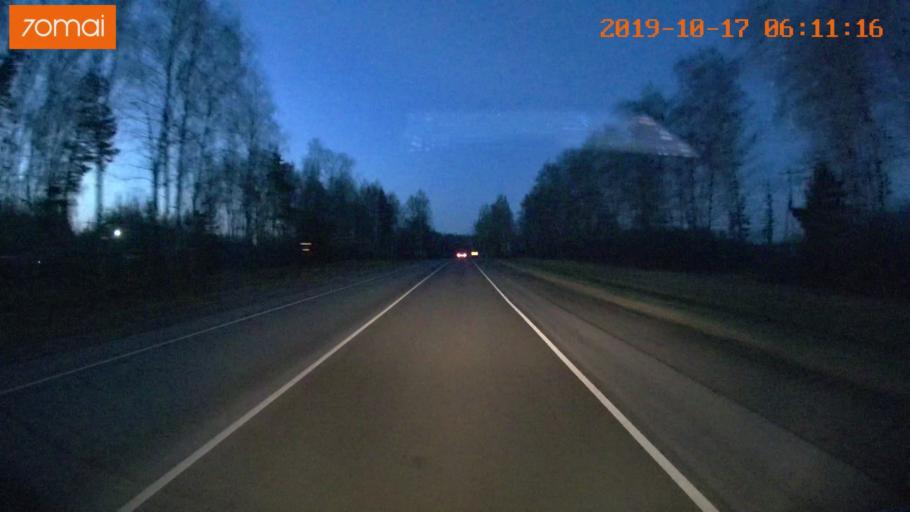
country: RU
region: Ivanovo
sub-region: Gorod Ivanovo
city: Ivanovo
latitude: 56.9218
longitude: 40.9586
